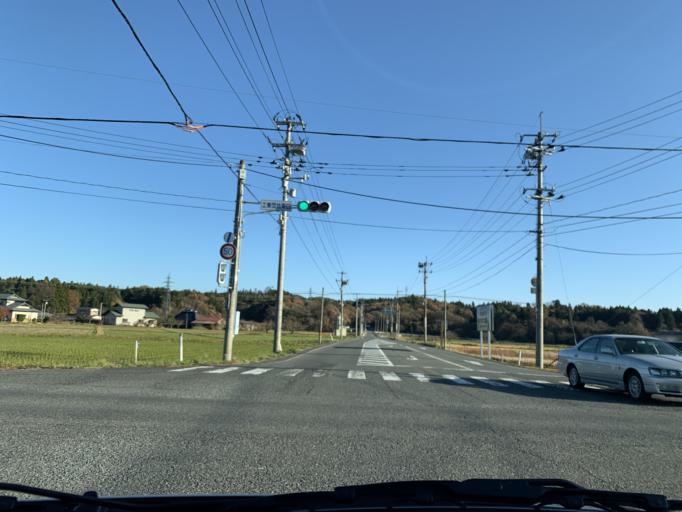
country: JP
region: Iwate
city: Mizusawa
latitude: 39.2033
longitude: 141.1895
